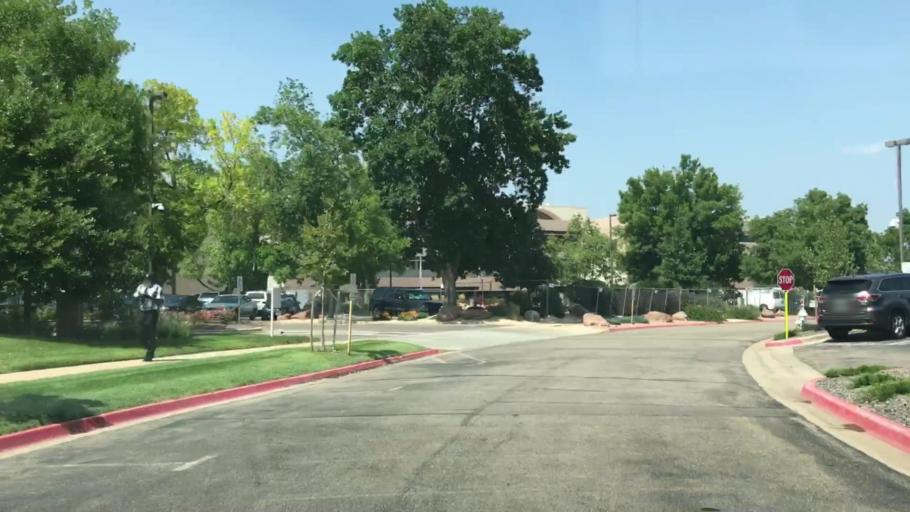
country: US
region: Colorado
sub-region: Boulder County
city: Gunbarrel
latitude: 40.0630
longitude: -105.2144
